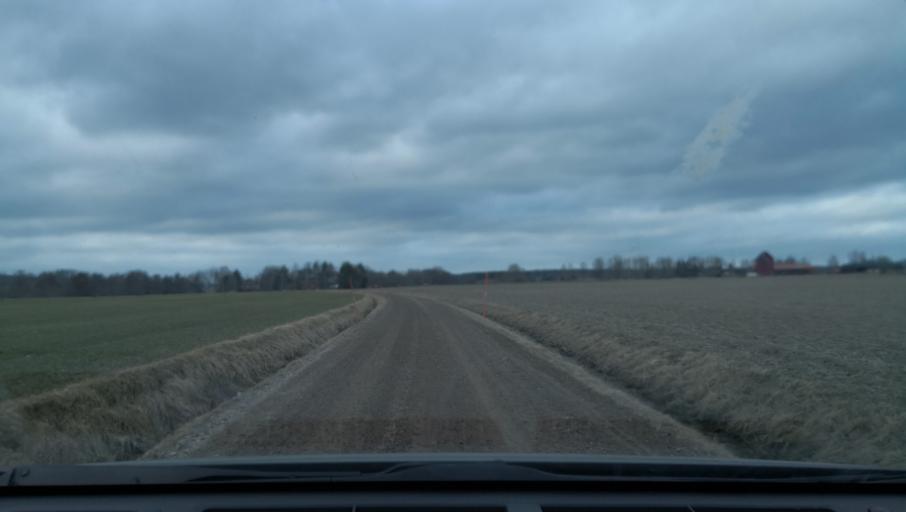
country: SE
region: Vaestmanland
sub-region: Kopings Kommun
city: Kolsva
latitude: 59.5363
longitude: 15.8945
